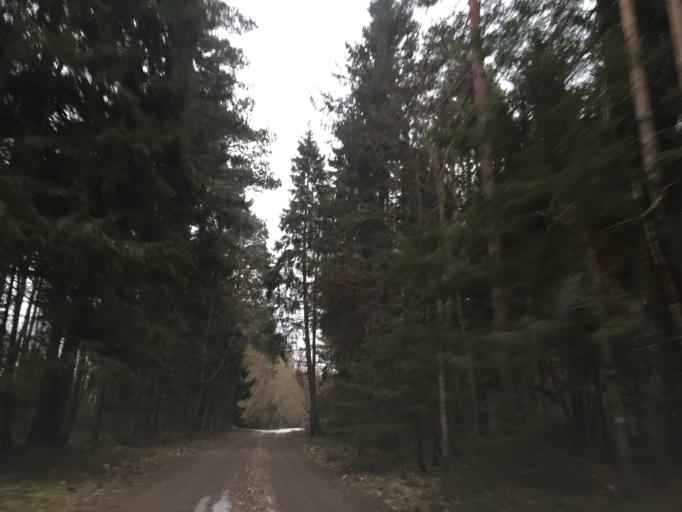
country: EE
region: Saare
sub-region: Kuressaare linn
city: Kuressaare
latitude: 58.3920
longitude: 22.2602
